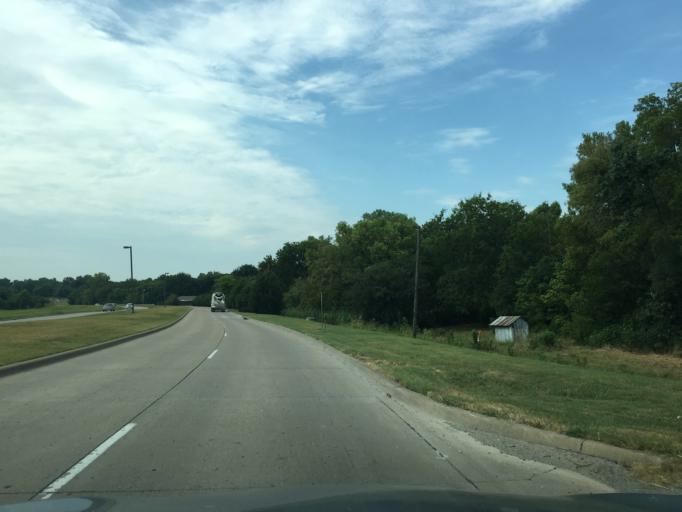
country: US
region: Texas
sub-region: Collin County
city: McKinney
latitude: 33.2018
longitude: -96.5999
